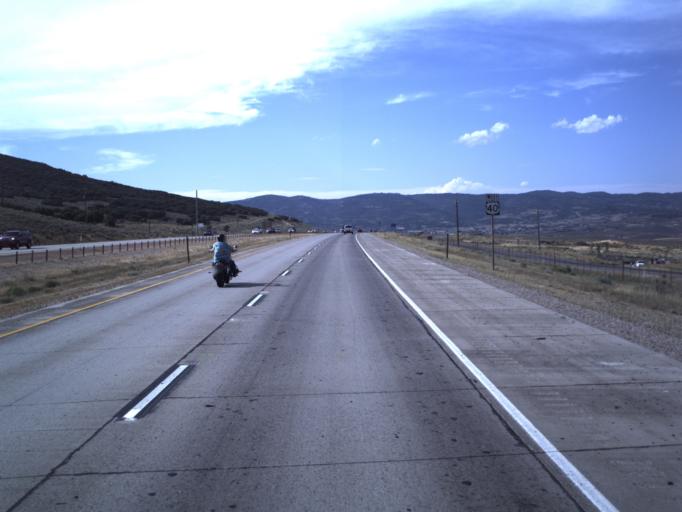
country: US
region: Utah
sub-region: Summit County
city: Park City
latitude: 40.6943
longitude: -111.4698
